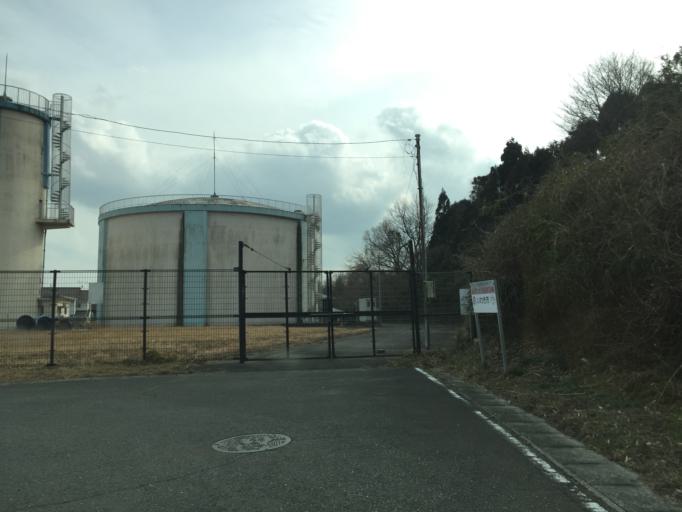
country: JP
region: Ibaraki
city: Kitaibaraki
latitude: 36.9340
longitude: 140.7423
